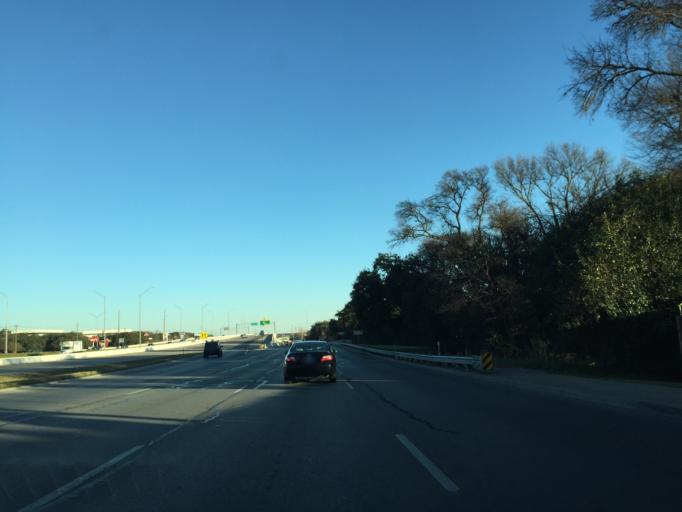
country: US
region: Texas
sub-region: Travis County
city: Austin
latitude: 30.3343
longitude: -97.6913
